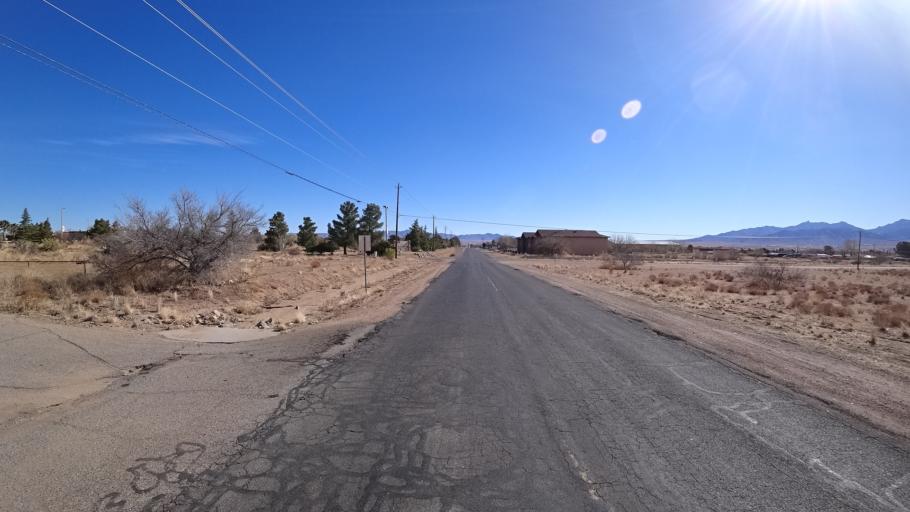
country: US
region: Arizona
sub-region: Mohave County
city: New Kingman-Butler
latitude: 35.2685
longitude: -114.0328
